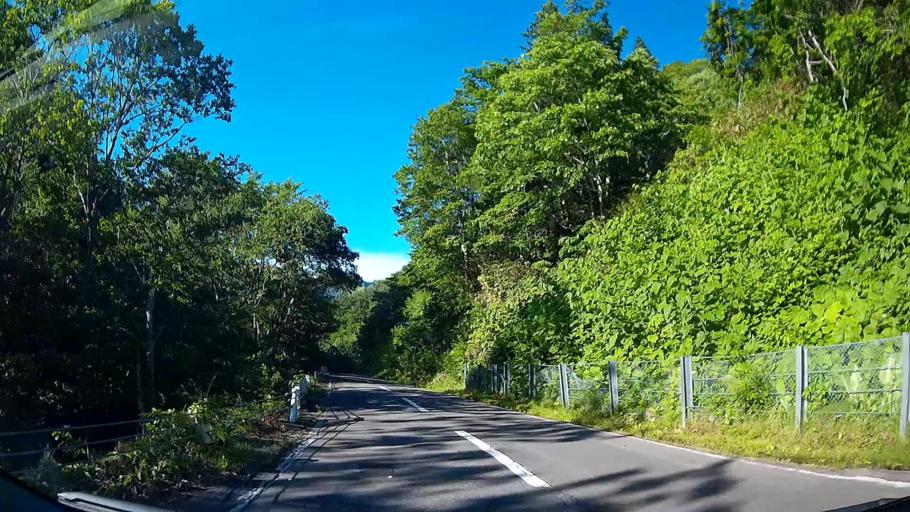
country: JP
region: Hokkaido
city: Otaru
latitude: 42.9865
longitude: 141.0749
